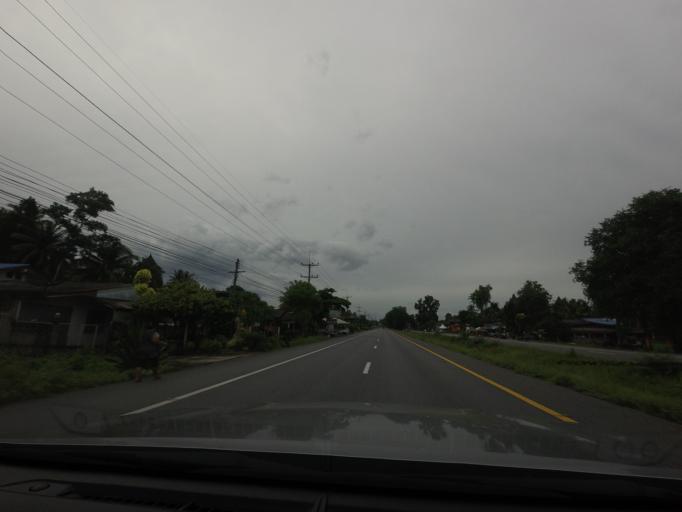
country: TH
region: Nakhon Si Thammarat
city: Chaloem Phra Kiat
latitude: 8.1662
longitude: 100.0495
